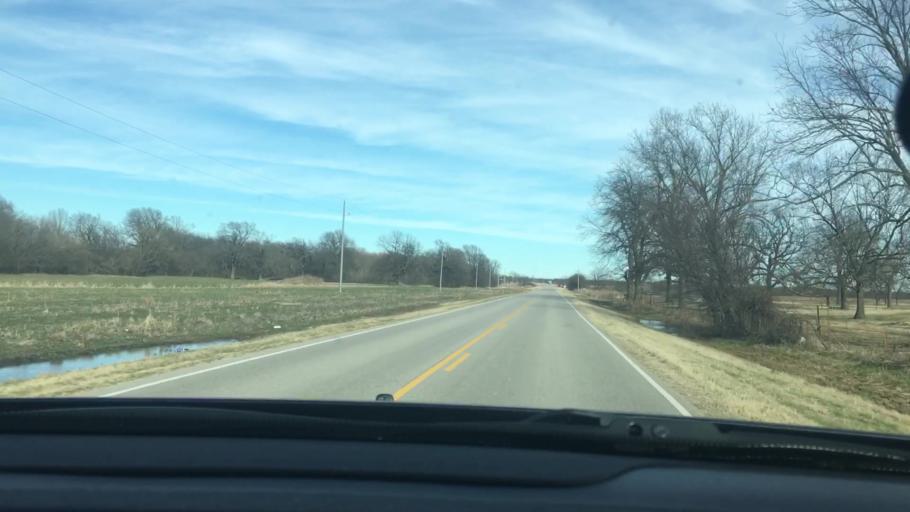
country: US
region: Oklahoma
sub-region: Murray County
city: Sulphur
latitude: 34.6346
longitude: -96.8182
